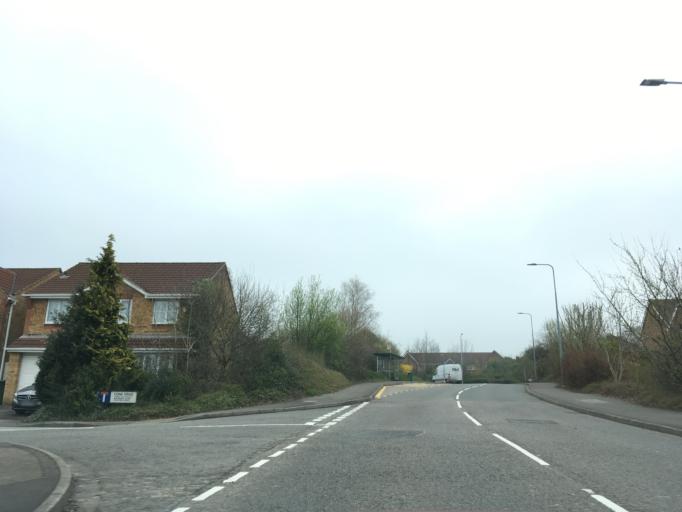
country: GB
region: Wales
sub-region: Caerphilly County Borough
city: Machen
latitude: 51.5357
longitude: -3.1350
